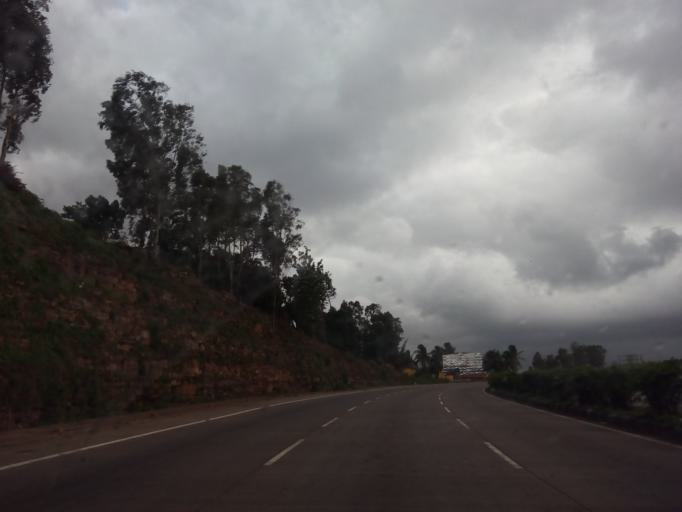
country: IN
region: Karnataka
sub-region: Belgaum
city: Belgaum
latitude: 16.0321
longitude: 74.5313
